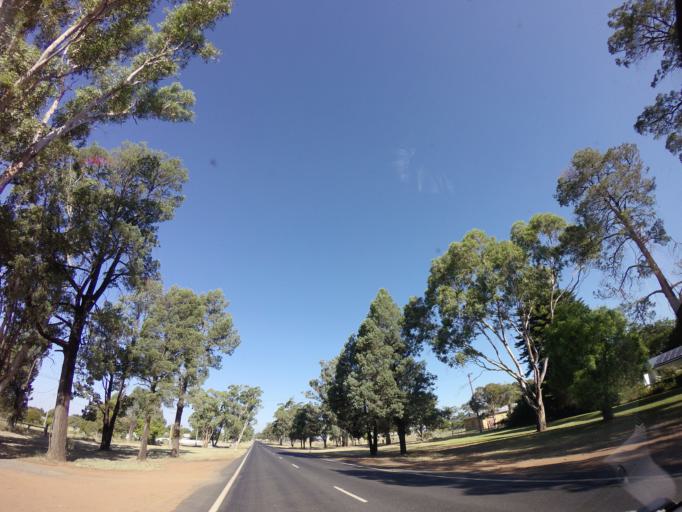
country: AU
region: New South Wales
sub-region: Gilgandra
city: Gilgandra
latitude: -31.7093
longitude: 148.6439
